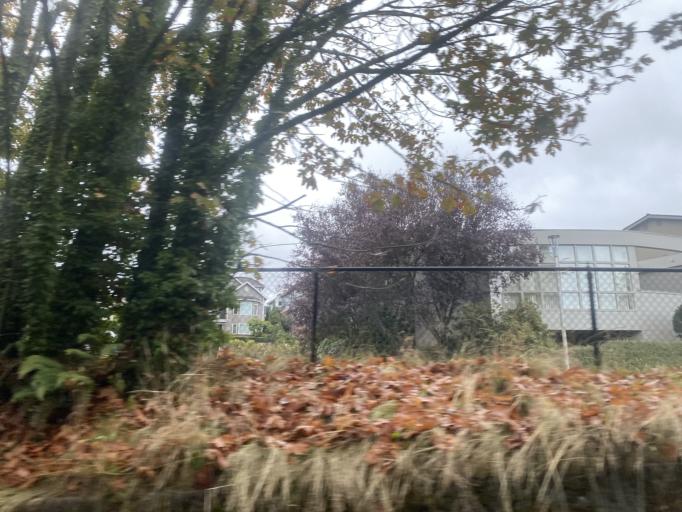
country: US
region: Washington
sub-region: King County
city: Seattle
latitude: 47.6434
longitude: -122.4139
